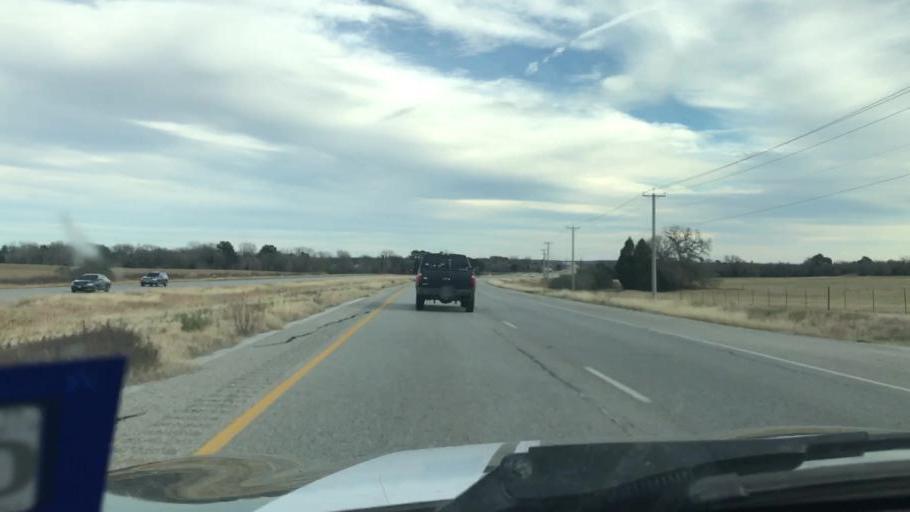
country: US
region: Texas
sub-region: Bastrop County
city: Elgin
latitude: 30.3214
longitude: -97.3198
